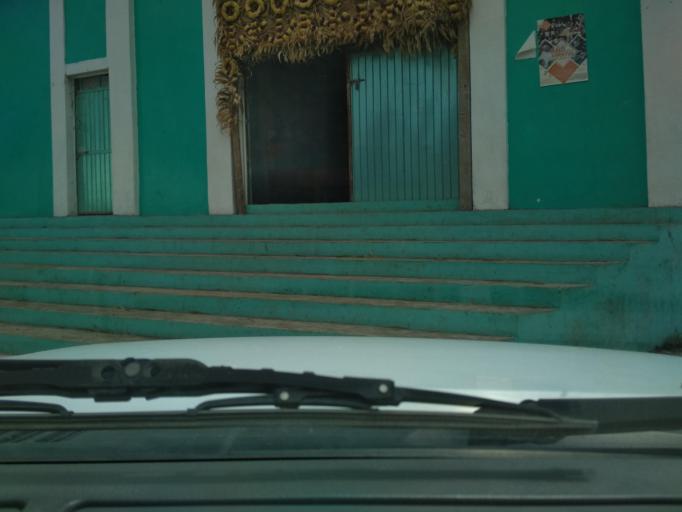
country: MX
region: Veracruz
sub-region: Camerino Z. Mendoza
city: Necoxtla
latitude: 18.7668
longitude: -97.1465
